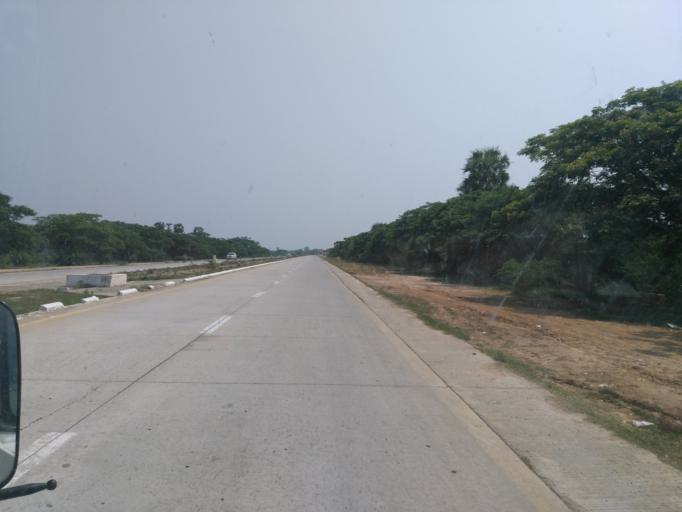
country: MM
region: Sagain
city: Sagaing
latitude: 21.8123
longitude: 95.9786
